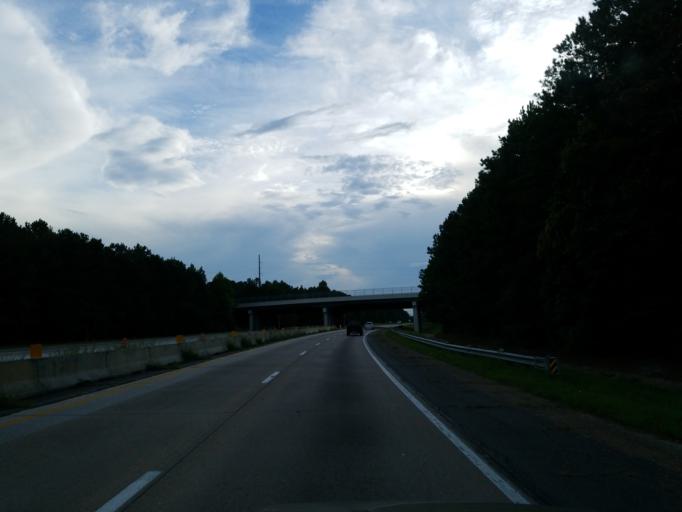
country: US
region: Georgia
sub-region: Forsyth County
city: Cumming
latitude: 34.1587
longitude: -84.1714
